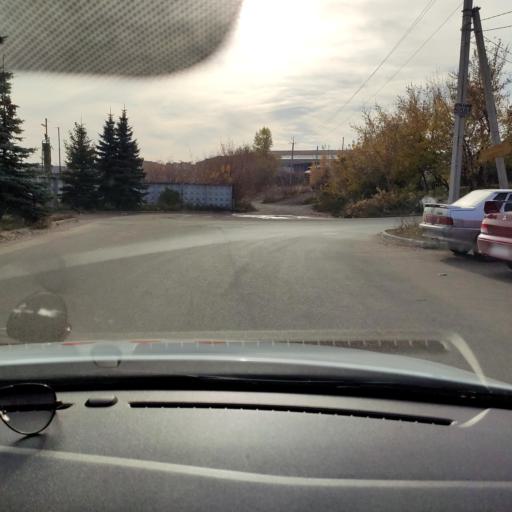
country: RU
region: Tatarstan
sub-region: Gorod Kazan'
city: Kazan
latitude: 55.8070
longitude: 49.0628
